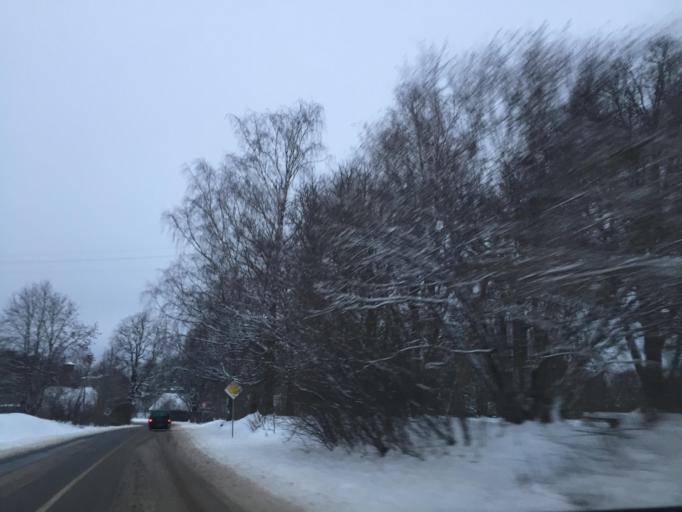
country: LV
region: Smiltene
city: Smiltene
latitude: 57.4366
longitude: 25.7888
